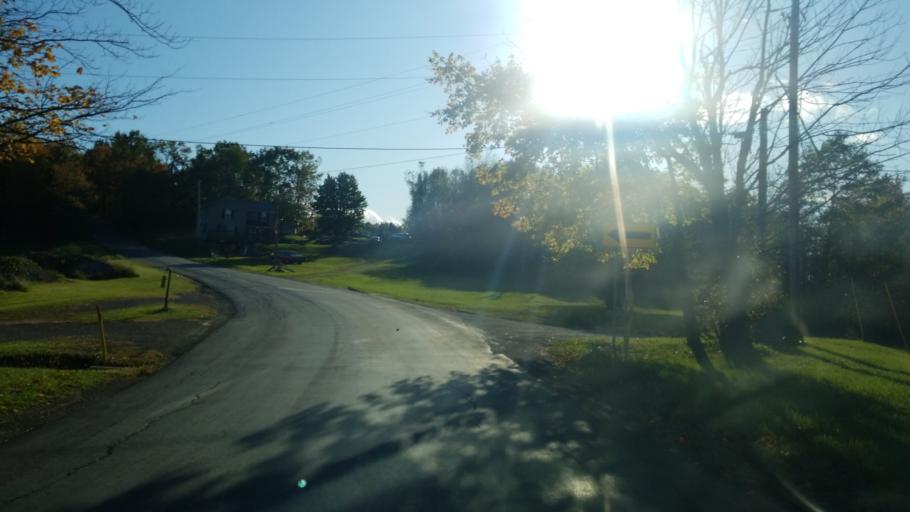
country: US
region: Pennsylvania
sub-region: Indiana County
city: Johnsonburg
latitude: 40.9030
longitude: -78.8785
